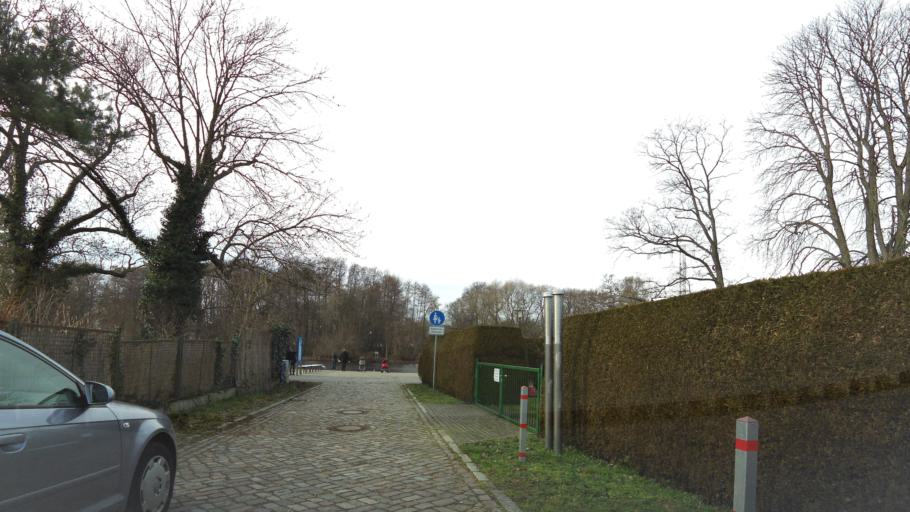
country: DE
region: Brandenburg
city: Michendorf
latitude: 52.3464
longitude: 12.9860
